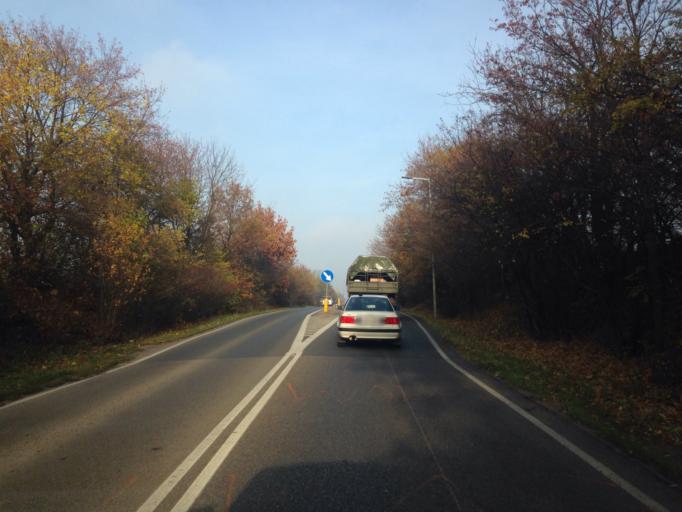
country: PL
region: Kujawsko-Pomorskie
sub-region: Powiat bydgoski
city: Osielsko
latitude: 53.1689
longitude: 18.0478
